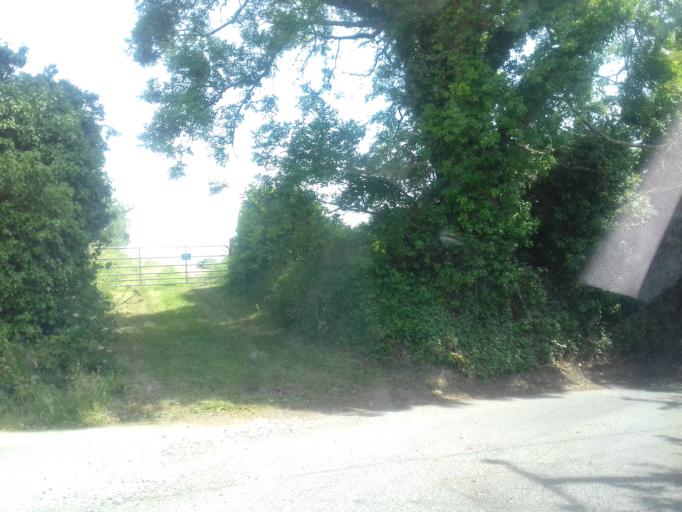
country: IE
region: Leinster
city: Lusk
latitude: 53.5224
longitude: -6.1382
